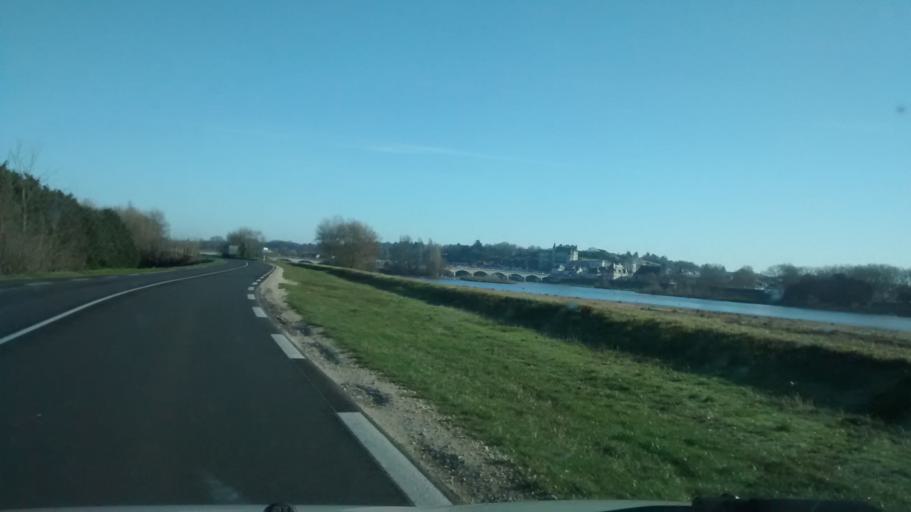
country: FR
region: Centre
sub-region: Departement d'Indre-et-Loire
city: Amboise
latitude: 47.4147
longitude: 0.9704
